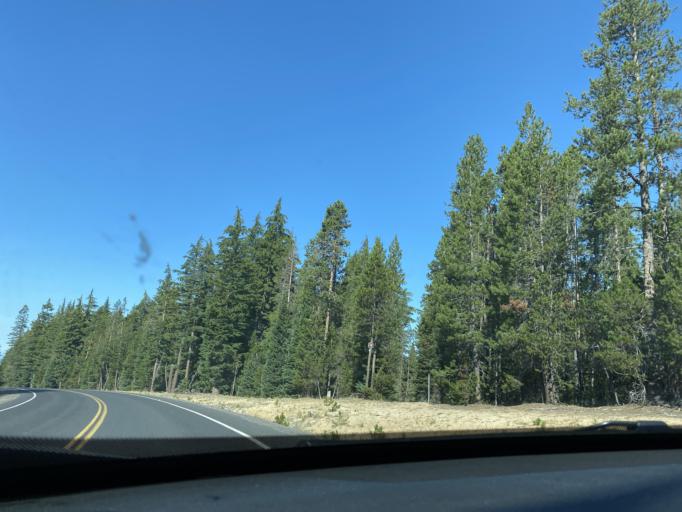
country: US
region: Oregon
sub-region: Deschutes County
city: Three Rivers
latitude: 43.7124
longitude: -121.2786
